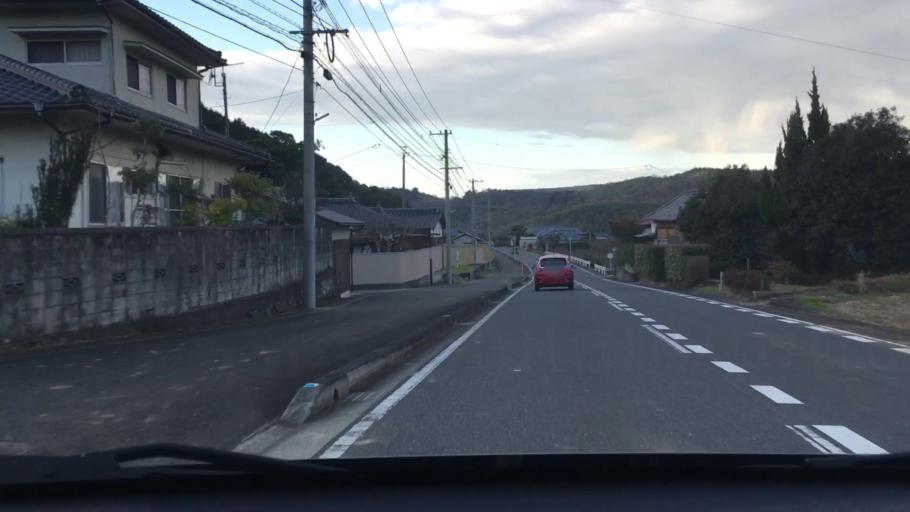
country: JP
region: Oita
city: Bungo-Takada-shi
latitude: 33.4972
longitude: 131.3770
